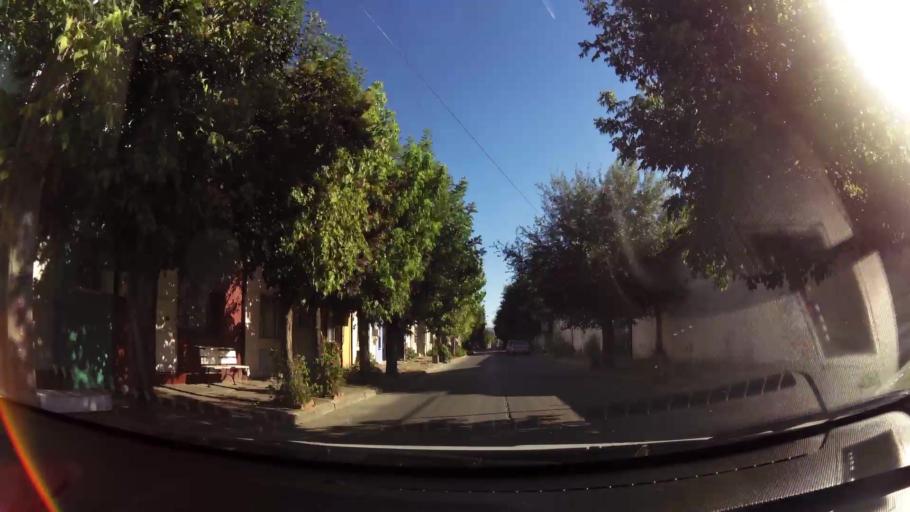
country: CL
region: O'Higgins
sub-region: Provincia de Colchagua
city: Chimbarongo
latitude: -34.5793
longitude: -70.9882
